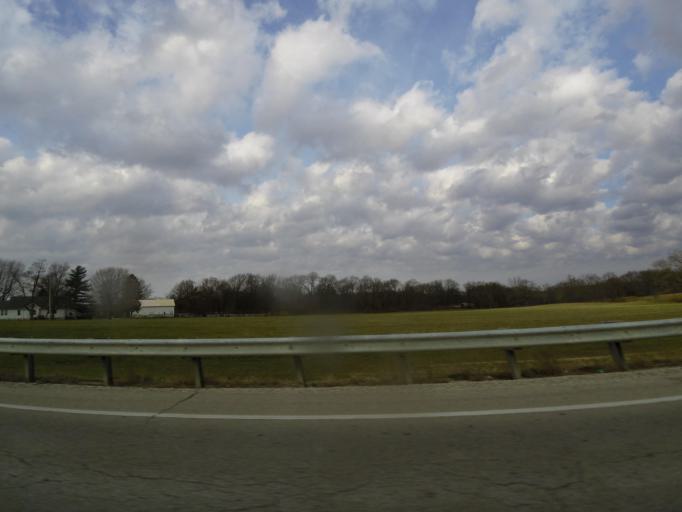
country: US
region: Illinois
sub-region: Christian County
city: Pana
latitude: 39.3011
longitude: -89.0888
